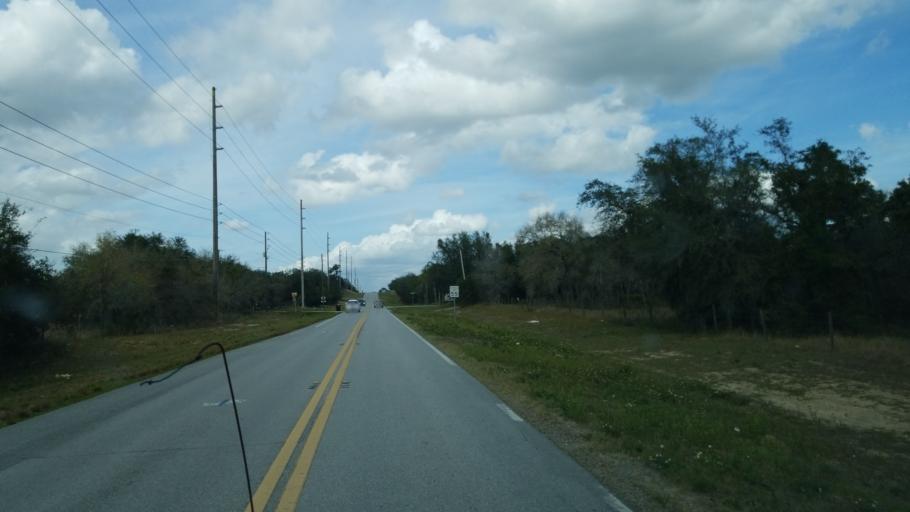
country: US
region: Florida
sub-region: Polk County
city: Lake Wales
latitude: 27.9533
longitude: -81.5378
